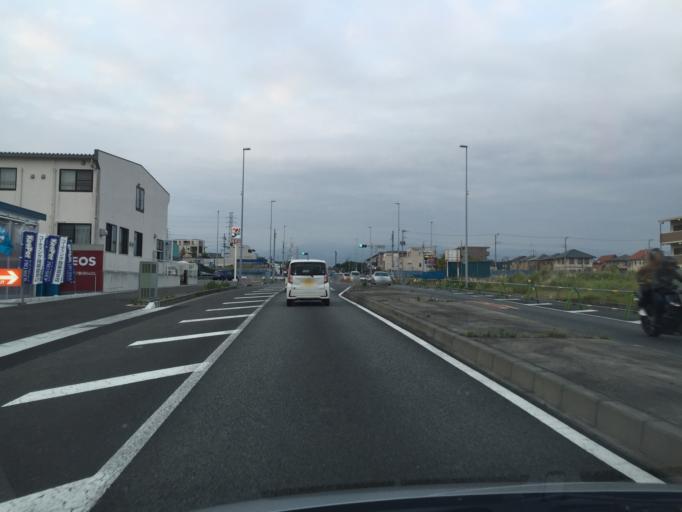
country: JP
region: Shizuoka
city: Numazu
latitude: 35.1303
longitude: 138.8714
